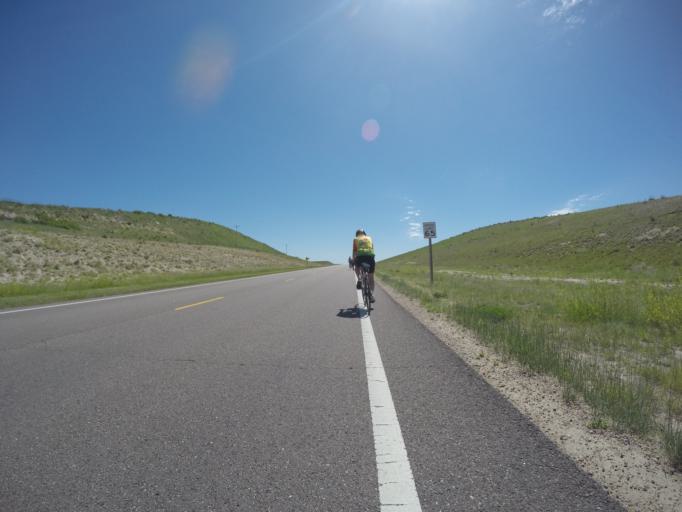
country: US
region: Kansas
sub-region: Rawlins County
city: Atwood
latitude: 39.8135
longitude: -100.9966
